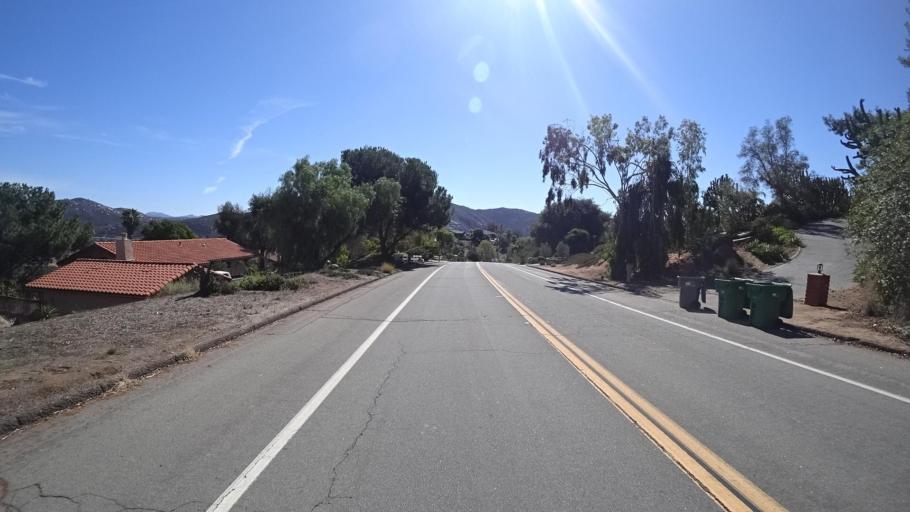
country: US
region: California
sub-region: San Diego County
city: Harbison Canyon
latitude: 32.8672
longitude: -116.8381
